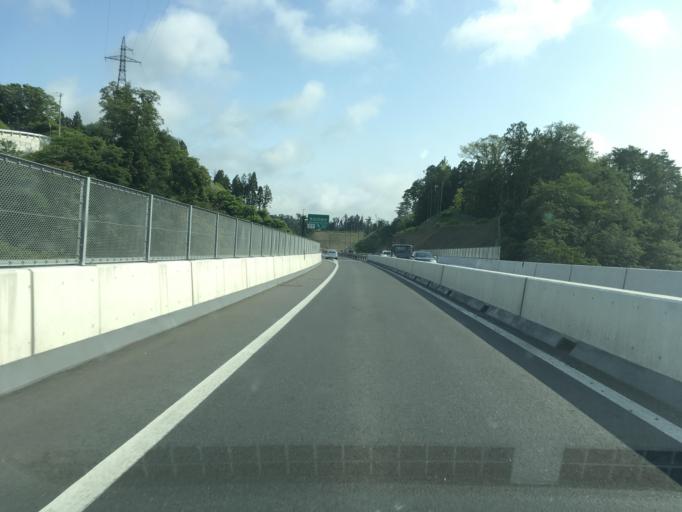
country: JP
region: Iwate
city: Ofunato
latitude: 38.9162
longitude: 141.5915
